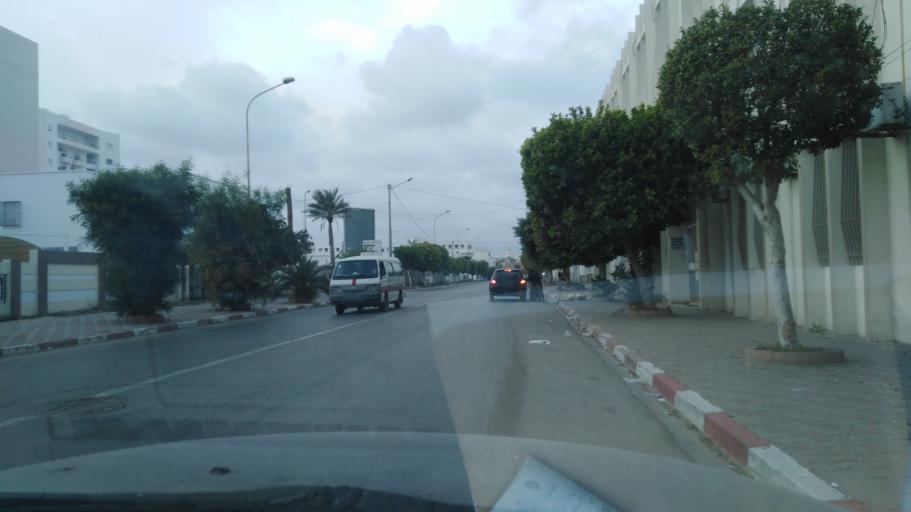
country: TN
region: Safaqis
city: Sfax
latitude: 34.7297
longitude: 10.7588
